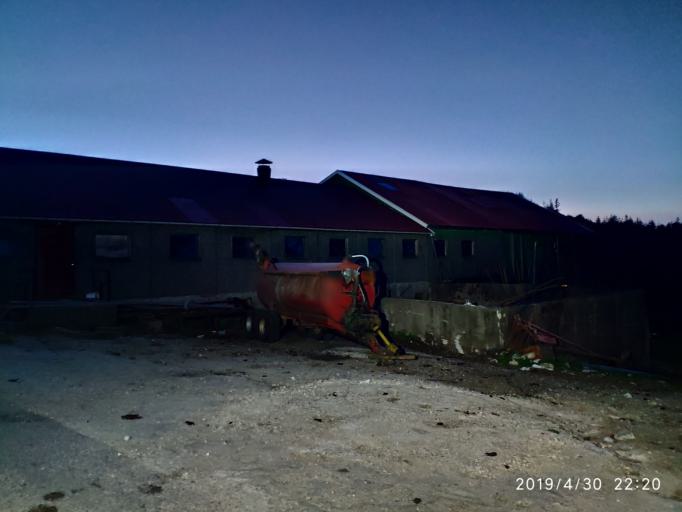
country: NO
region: Rogaland
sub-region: Eigersund
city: Egersund
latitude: 58.4811
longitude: 6.0104
